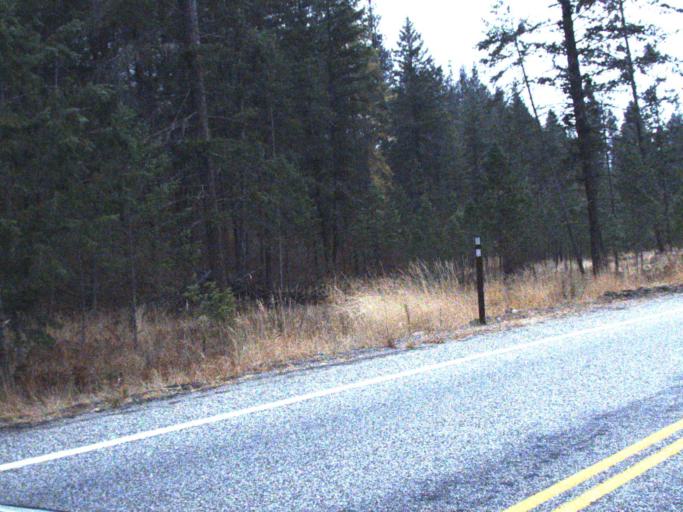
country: US
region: Washington
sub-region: Stevens County
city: Kettle Falls
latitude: 48.7821
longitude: -118.1482
